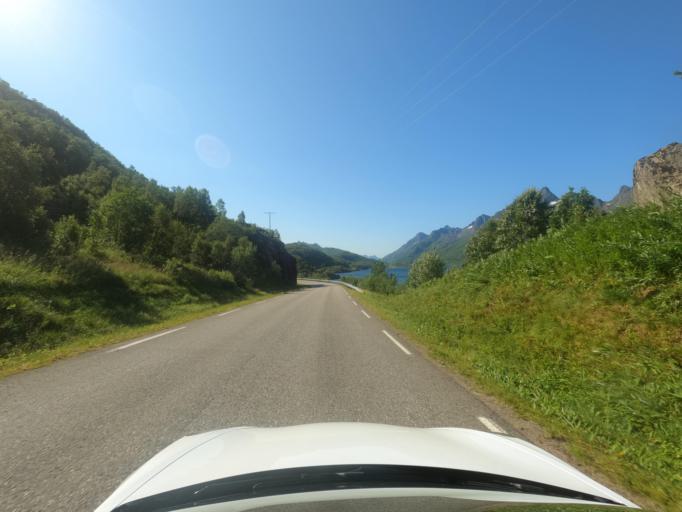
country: NO
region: Nordland
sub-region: Hadsel
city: Stokmarknes
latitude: 68.4494
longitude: 15.2039
